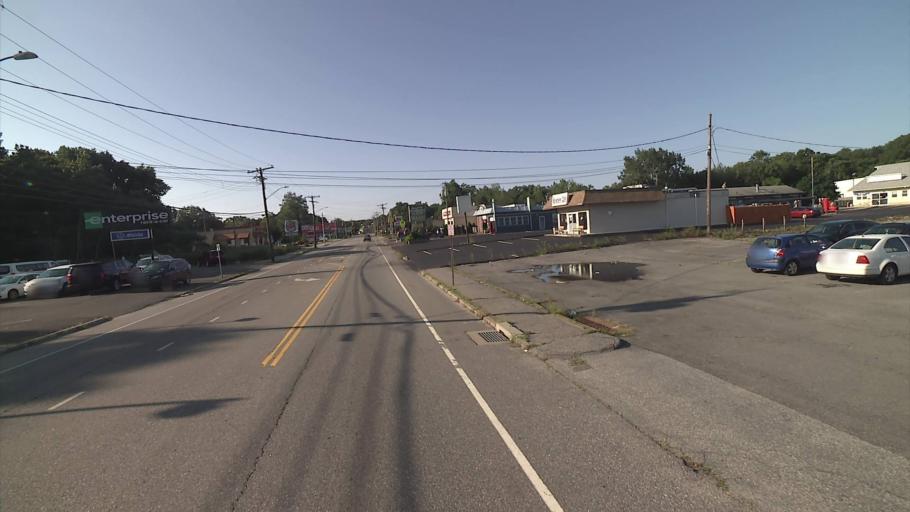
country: US
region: Connecticut
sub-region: New London County
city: New London
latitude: 41.3620
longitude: -72.1162
